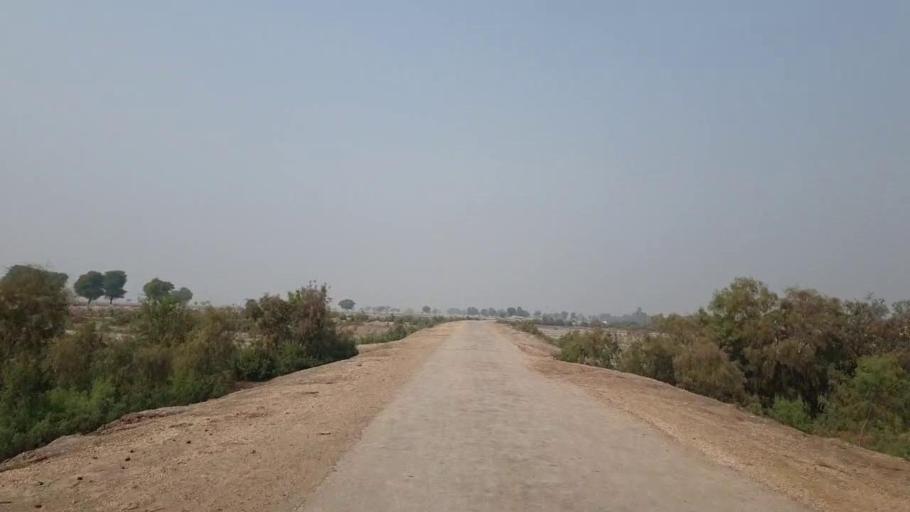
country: PK
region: Sindh
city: Bhan
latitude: 26.5055
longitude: 67.6907
